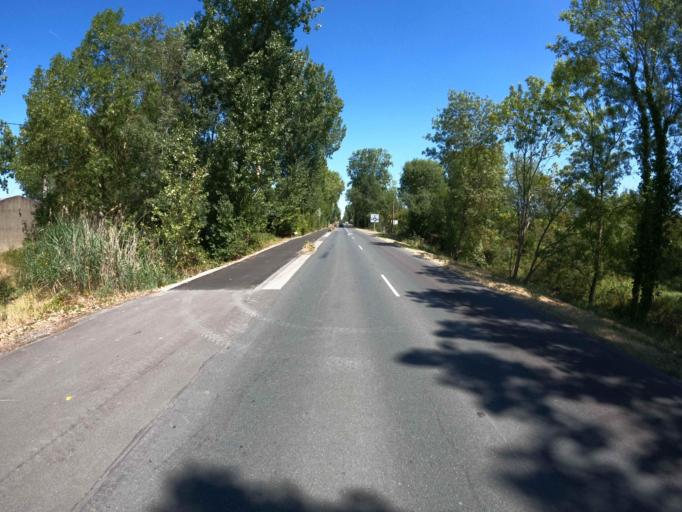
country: FR
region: Pays de la Loire
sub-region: Departement de la Vendee
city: Le Perrier
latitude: 46.8069
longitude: -2.0221
